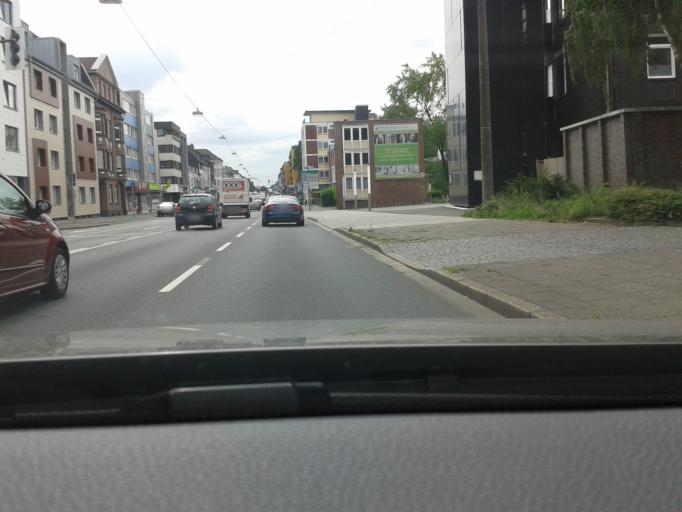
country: DE
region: North Rhine-Westphalia
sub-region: Regierungsbezirk Dusseldorf
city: Oberhausen
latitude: 51.4780
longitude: 6.8636
